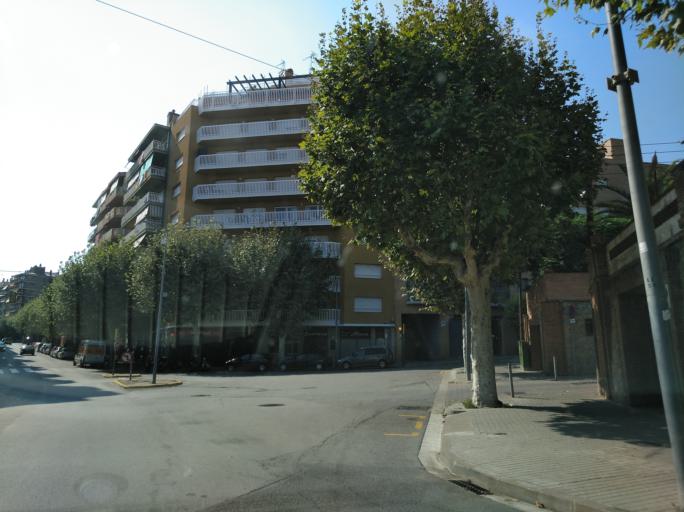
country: ES
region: Catalonia
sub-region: Provincia de Barcelona
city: Mataro
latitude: 41.5458
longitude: 2.4476
